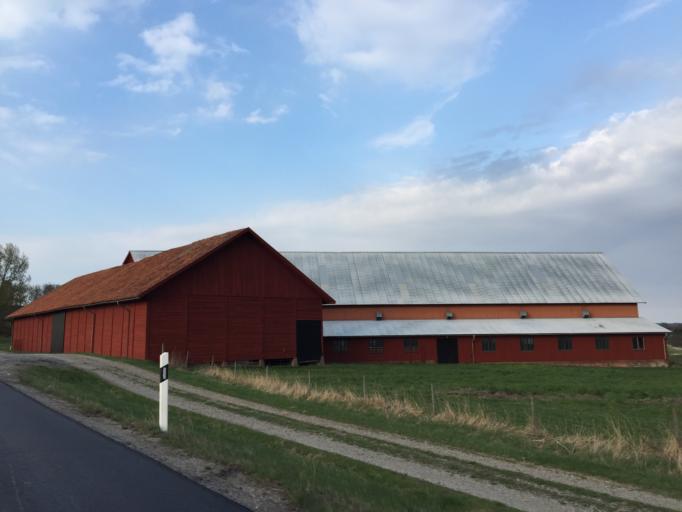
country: SE
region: Soedermanland
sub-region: Trosa Kommun
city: Vagnharad
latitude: 59.0337
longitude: 17.5979
